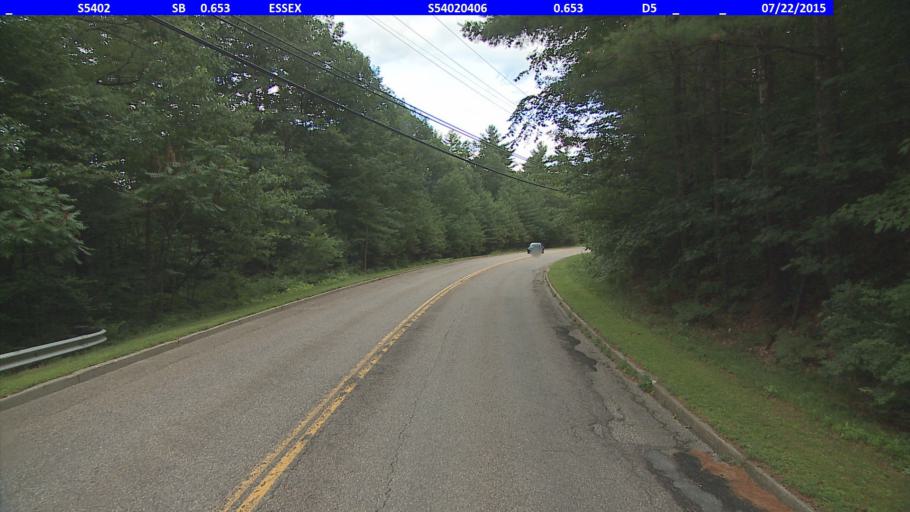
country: US
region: Vermont
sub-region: Chittenden County
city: Williston
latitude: 44.4880
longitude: -73.0496
